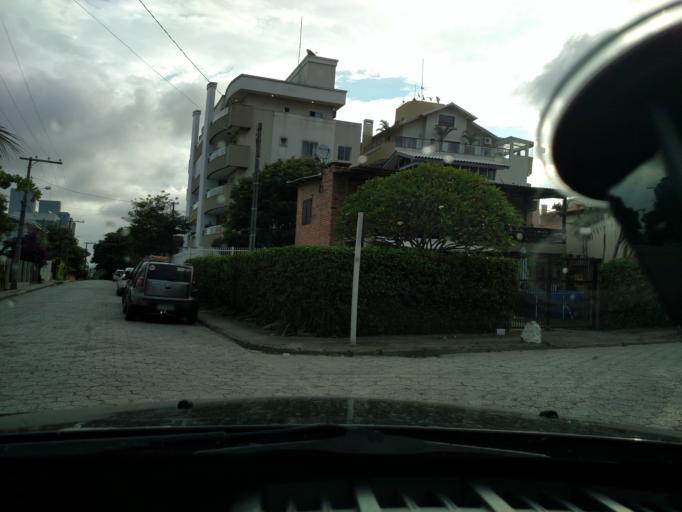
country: BR
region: Santa Catarina
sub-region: Porto Belo
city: Porto Belo
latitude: -27.1415
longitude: -48.5094
